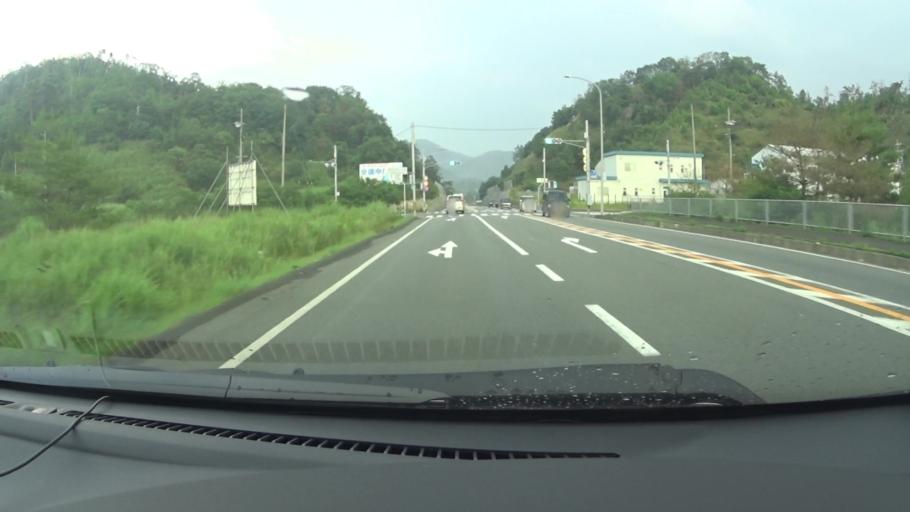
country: JP
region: Kyoto
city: Ayabe
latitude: 35.2125
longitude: 135.4324
